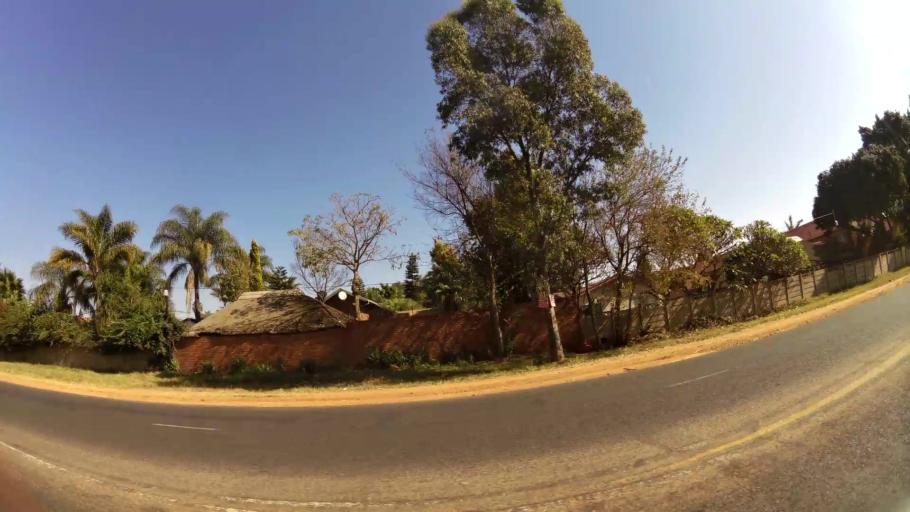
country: ZA
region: North-West
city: Ga-Rankuwa
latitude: -25.6446
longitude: 28.1028
